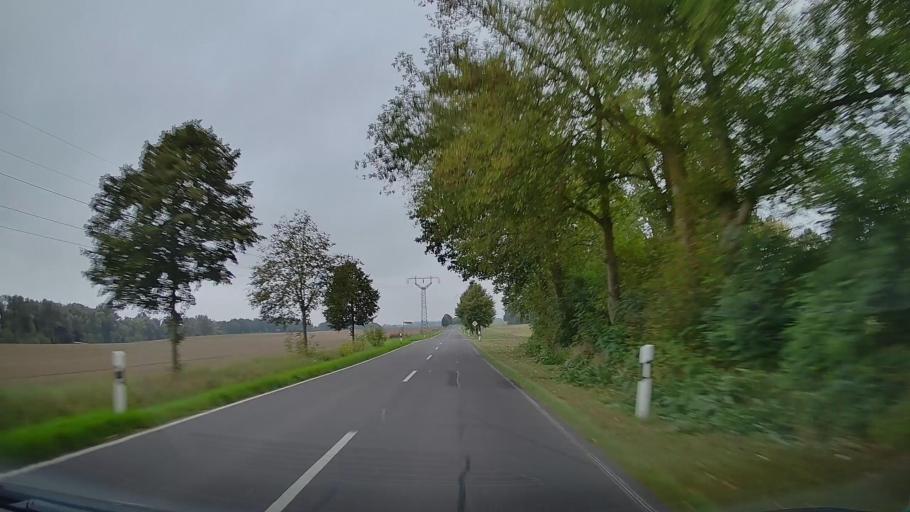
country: DE
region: Mecklenburg-Vorpommern
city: Guestrow
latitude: 53.8056
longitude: 12.1090
